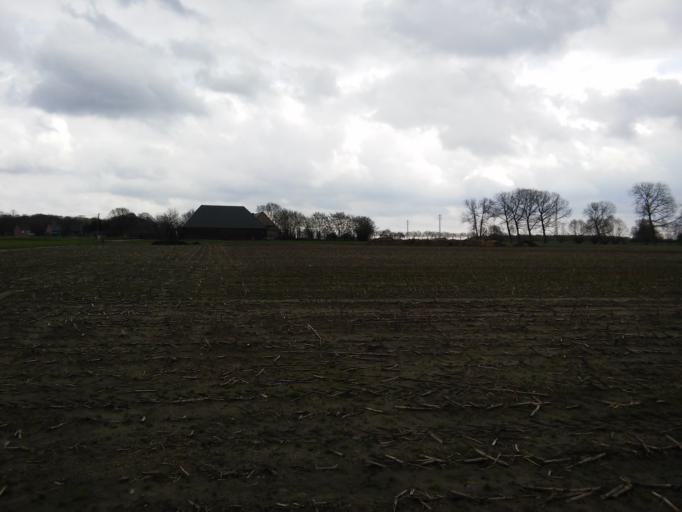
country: BE
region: Flanders
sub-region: Provincie Antwerpen
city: Rumst
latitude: 51.0987
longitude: 4.4082
